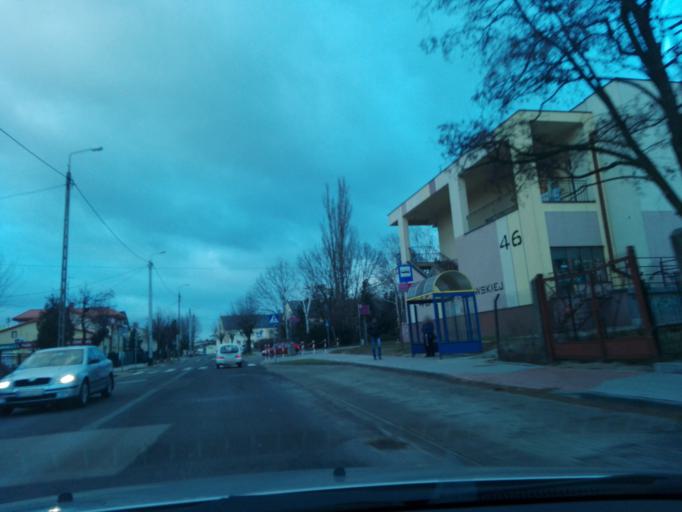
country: PL
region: Lodz Voivodeship
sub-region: Powiat kutnowski
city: Kutno
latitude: 52.2406
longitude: 19.3530
